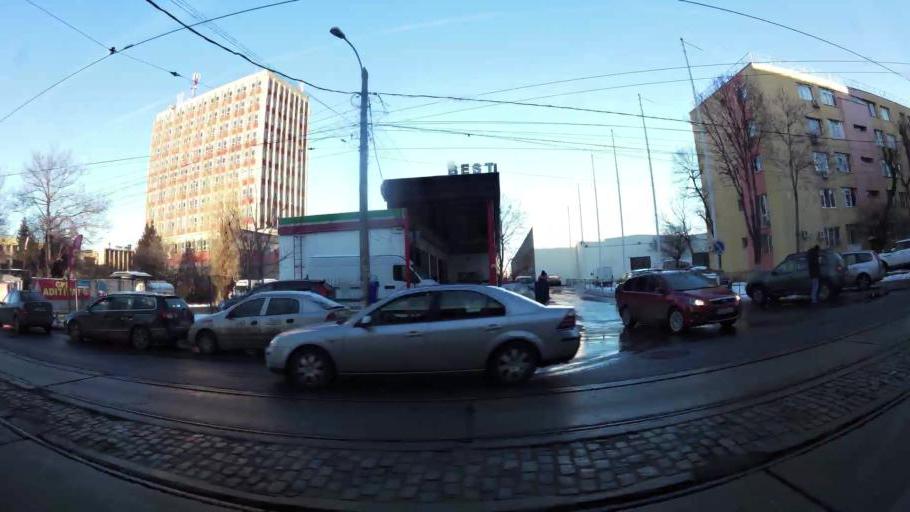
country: RO
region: Bucuresti
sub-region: Municipiul Bucuresti
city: Bucharest
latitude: 44.4478
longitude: 26.1324
